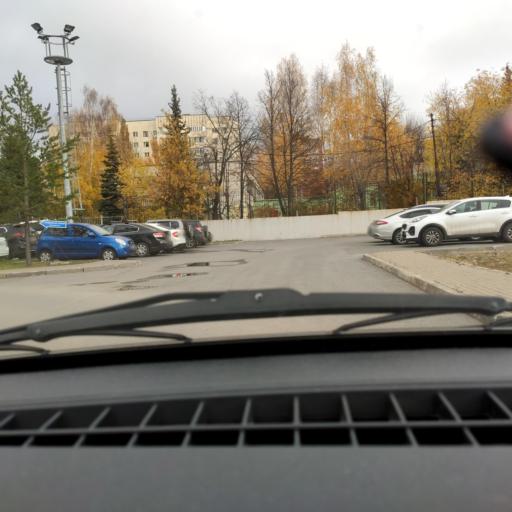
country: RU
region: Bashkortostan
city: Ufa
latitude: 54.7386
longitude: 56.0226
